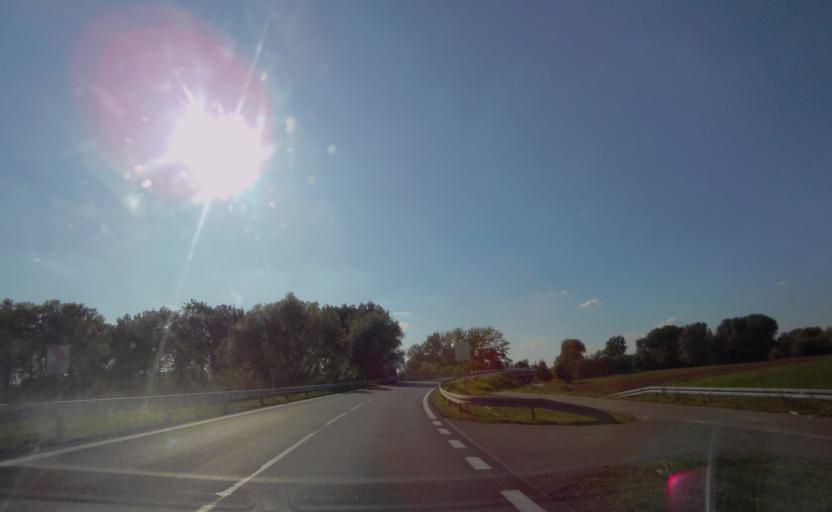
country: PL
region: Subcarpathian Voivodeship
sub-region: Powiat lezajski
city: Stare Miasto
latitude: 50.2912
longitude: 22.4450
